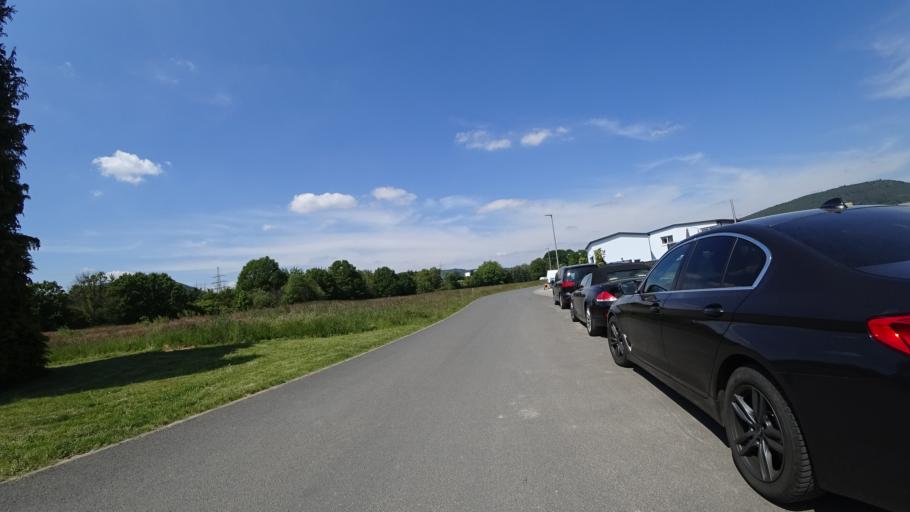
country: DE
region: Bavaria
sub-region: Regierungsbezirk Unterfranken
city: Kleinheubach
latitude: 49.7041
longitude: 9.2240
